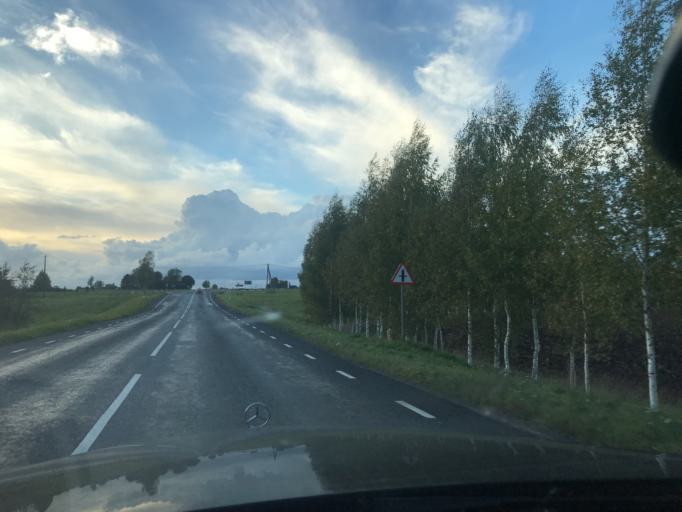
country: EE
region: Vorumaa
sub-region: Antsla vald
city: Vana-Antsla
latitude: 57.8840
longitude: 26.5300
